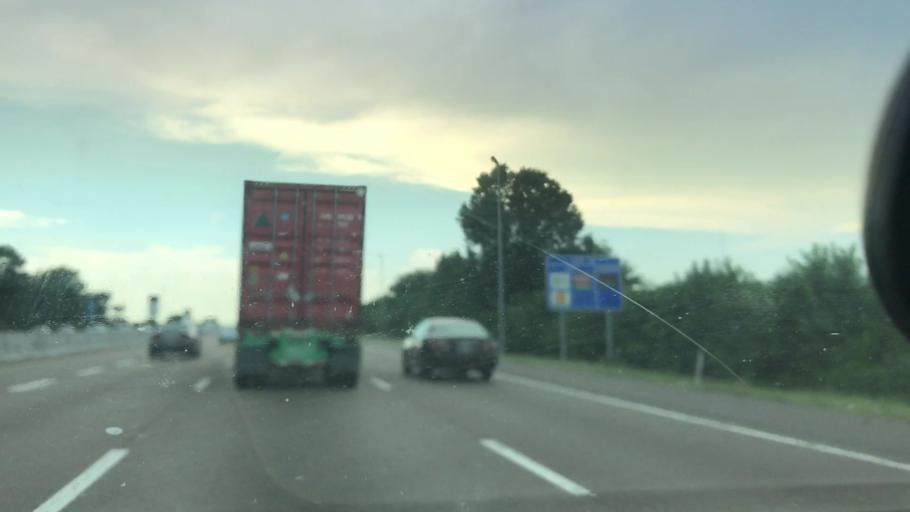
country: US
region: Tennessee
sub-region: Shelby County
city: Bartlett
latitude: 35.1682
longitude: -89.8553
